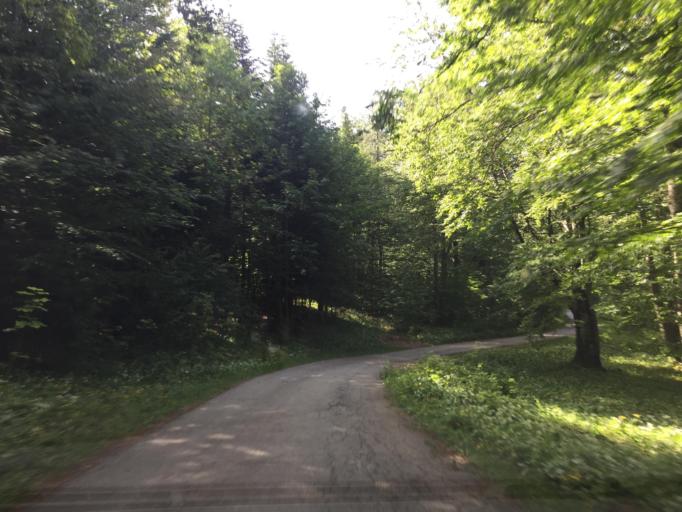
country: HR
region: Primorsko-Goranska
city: Podhum
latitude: 45.4371
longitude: 14.5628
